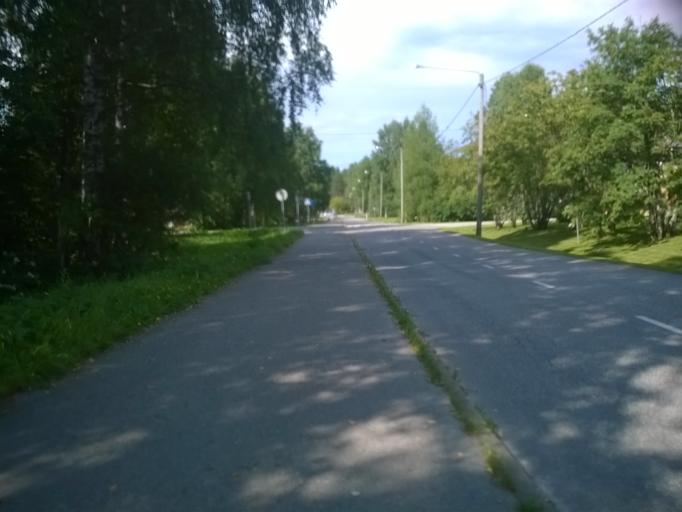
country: FI
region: Kainuu
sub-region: Kehys-Kainuu
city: Kuhmo
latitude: 64.1290
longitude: 29.5280
